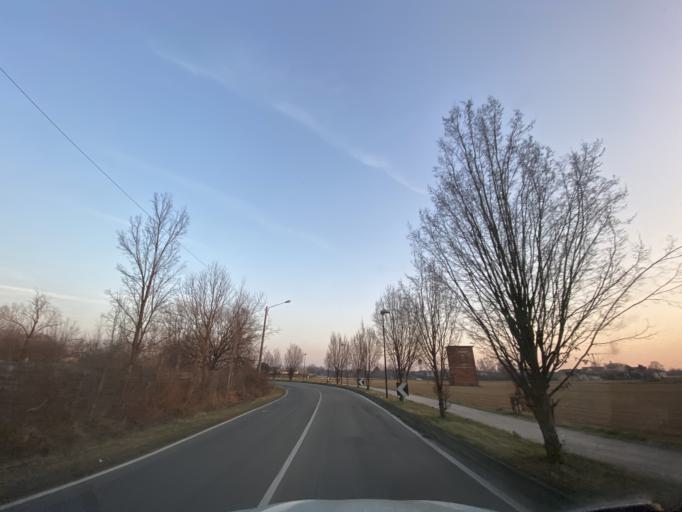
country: IT
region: Lombardy
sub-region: Provincia di Monza e Brianza
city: Villaggio del Sole
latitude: 45.6102
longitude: 9.1127
